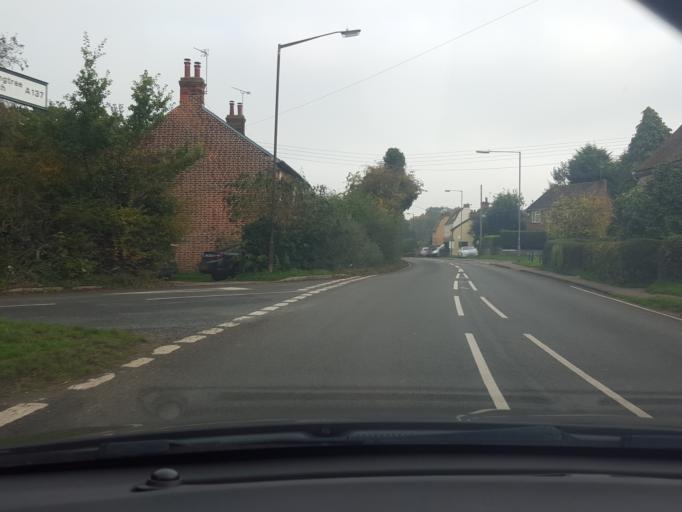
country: GB
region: England
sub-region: Essex
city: Manningtree
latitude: 51.9399
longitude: 1.0314
